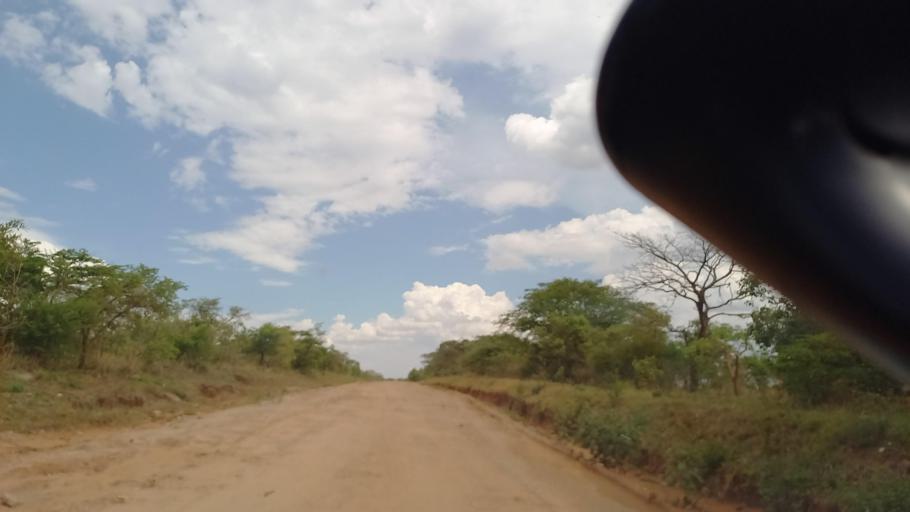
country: ZM
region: Southern
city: Nakambala
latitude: -16.0493
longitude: 27.9813
